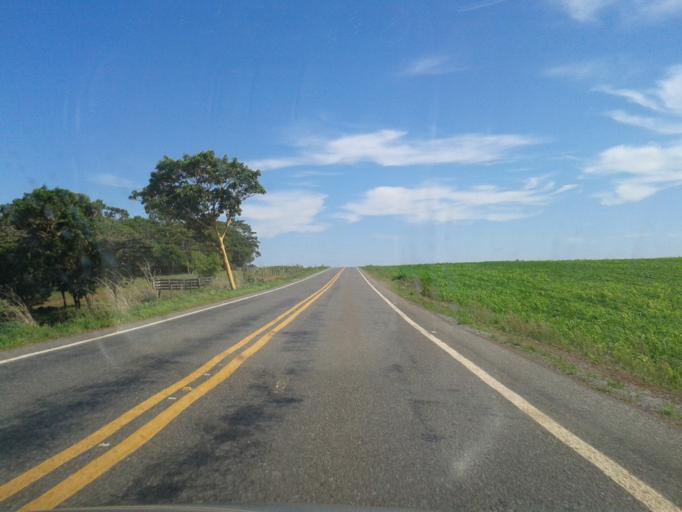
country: BR
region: Goias
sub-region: Piracanjuba
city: Piracanjuba
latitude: -17.3236
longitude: -48.8008
